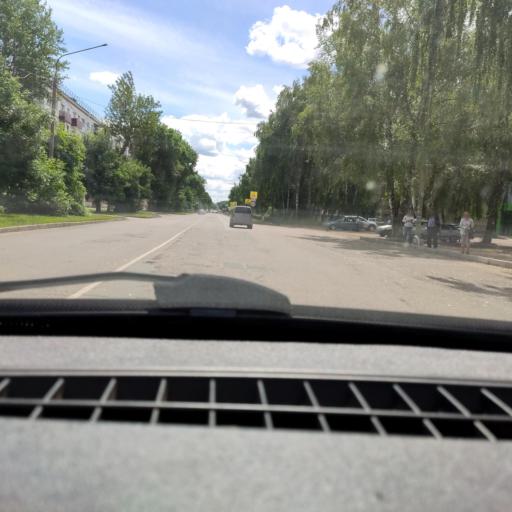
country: RU
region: Bashkortostan
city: Sterlitamak
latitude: 53.6427
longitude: 55.9335
